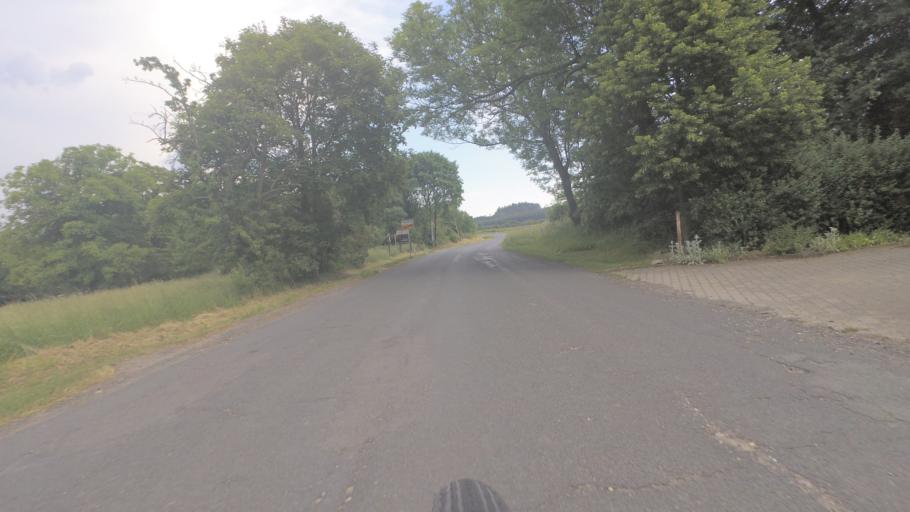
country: DE
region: Saxony-Anhalt
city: Ballenstedt
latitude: 51.7121
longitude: 11.3016
